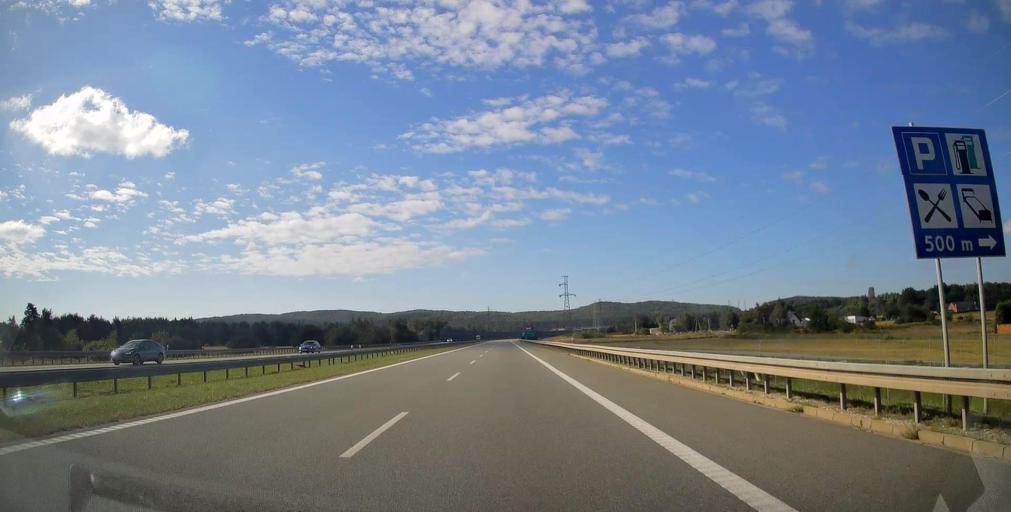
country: PL
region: Swietokrzyskie
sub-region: Powiat kielecki
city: Piekoszow
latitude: 50.8644
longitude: 20.5121
